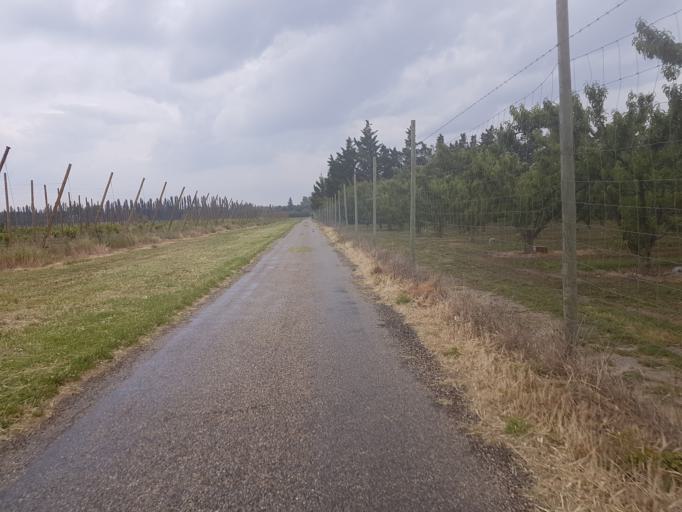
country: FR
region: Languedoc-Roussillon
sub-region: Departement du Gard
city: Villeneuve-les-Avignon
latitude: 43.9713
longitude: 4.8222
